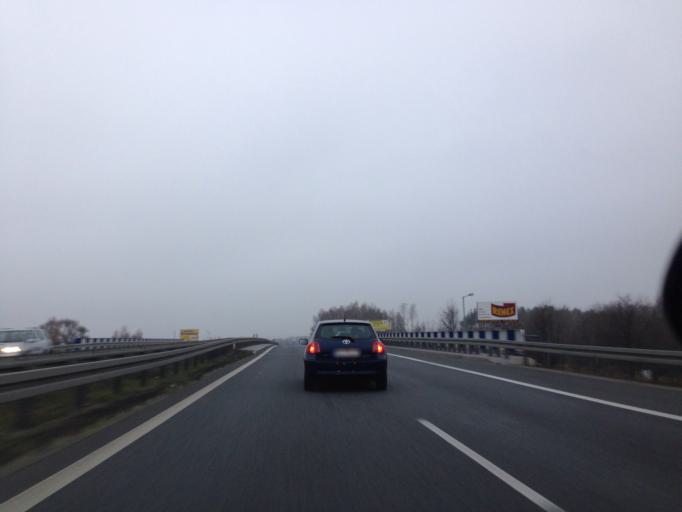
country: PL
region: Lodz Voivodeship
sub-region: Powiat lodzki wschodni
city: Starowa Gora
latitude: 51.6754
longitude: 19.4758
